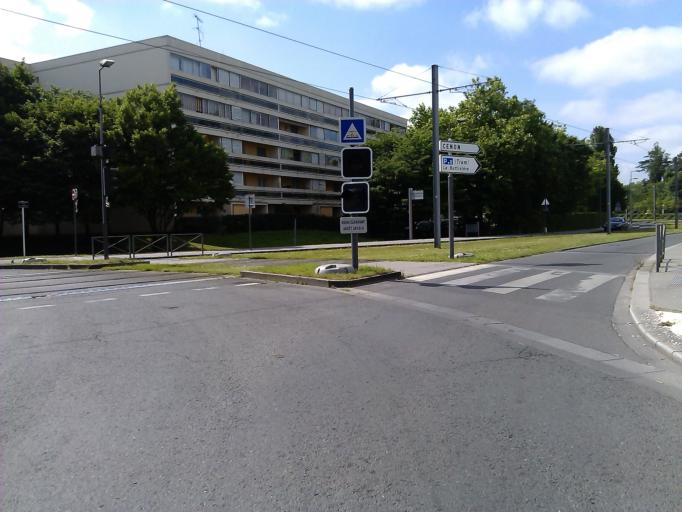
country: FR
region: Aquitaine
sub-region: Departement de la Gironde
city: Lormont
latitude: 44.8678
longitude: -0.5237
